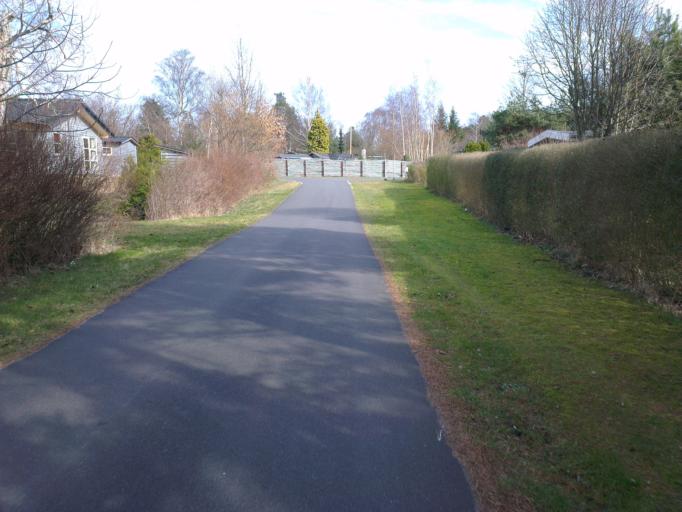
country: DK
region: Capital Region
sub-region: Halsnaes Kommune
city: Hundested
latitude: 55.9240
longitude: 11.9104
